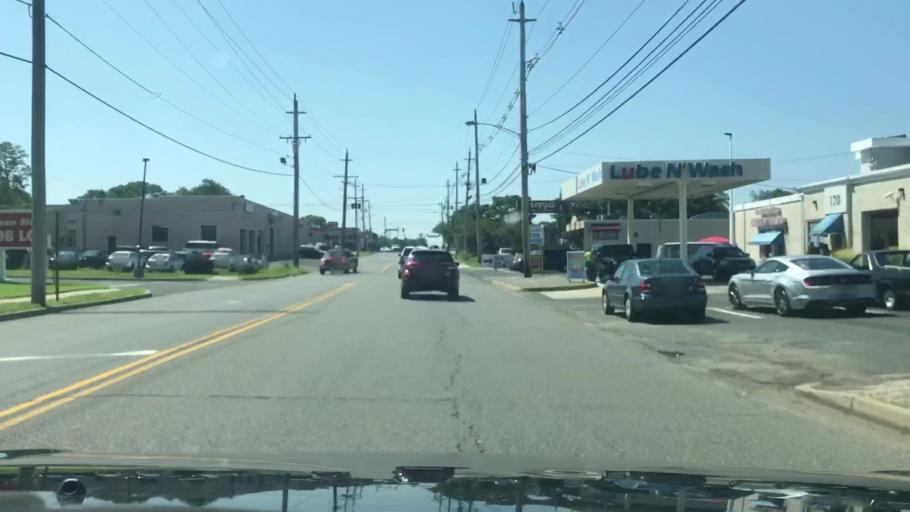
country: US
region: New Jersey
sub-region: Monmouth County
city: Red Bank
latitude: 40.3376
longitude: -74.0719
